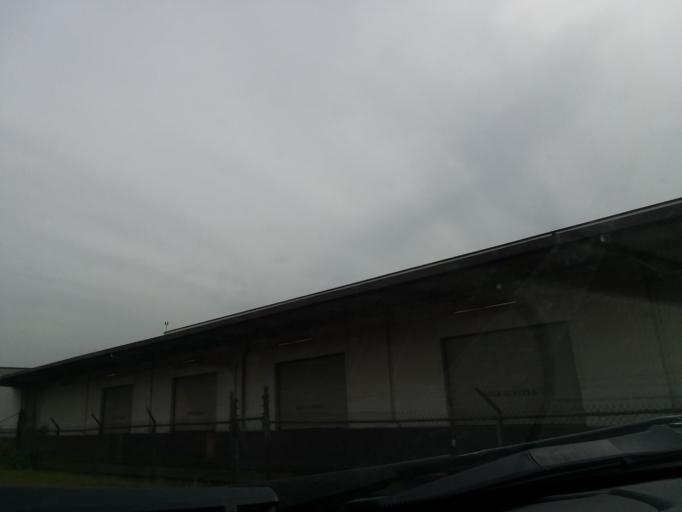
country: US
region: Washington
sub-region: King County
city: Riverton
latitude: 47.5115
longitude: -122.2870
